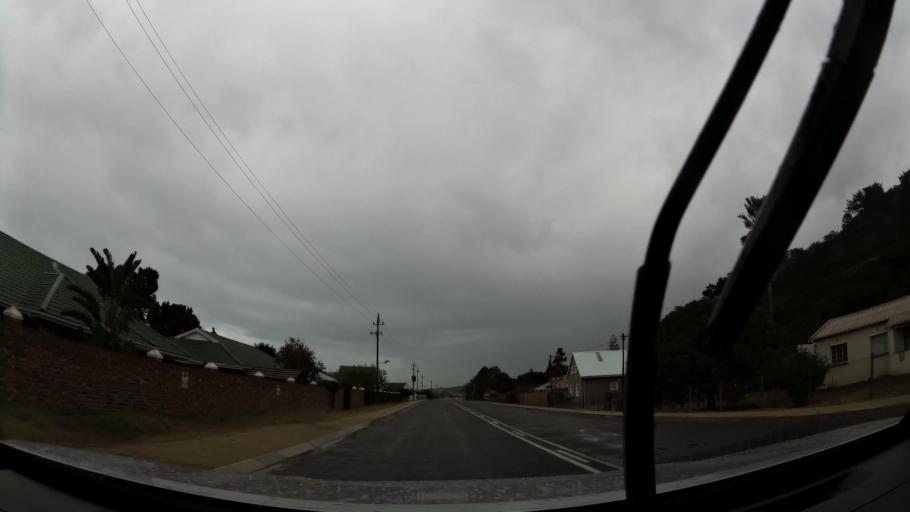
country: ZA
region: Western Cape
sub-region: Eden District Municipality
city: Mossel Bay
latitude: -34.0497
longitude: 22.2381
